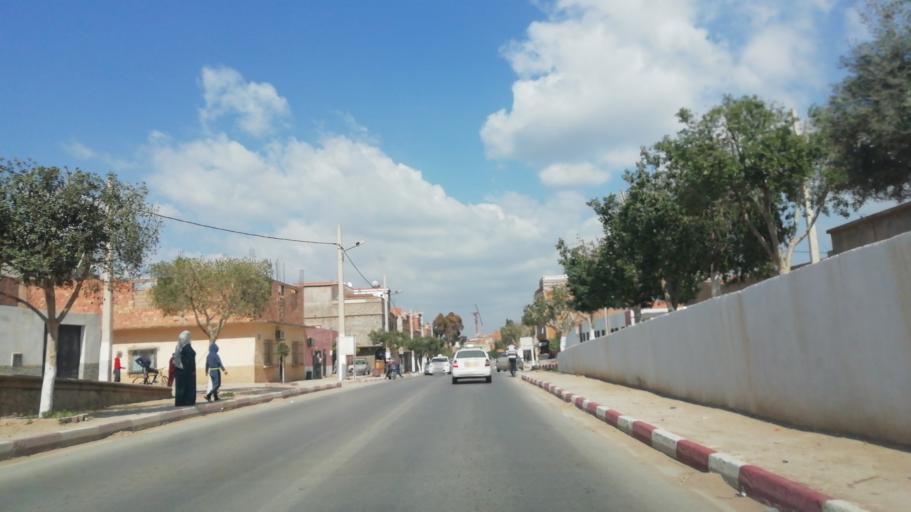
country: DZ
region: Mascara
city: Mascara
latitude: 35.5724
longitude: 0.0690
